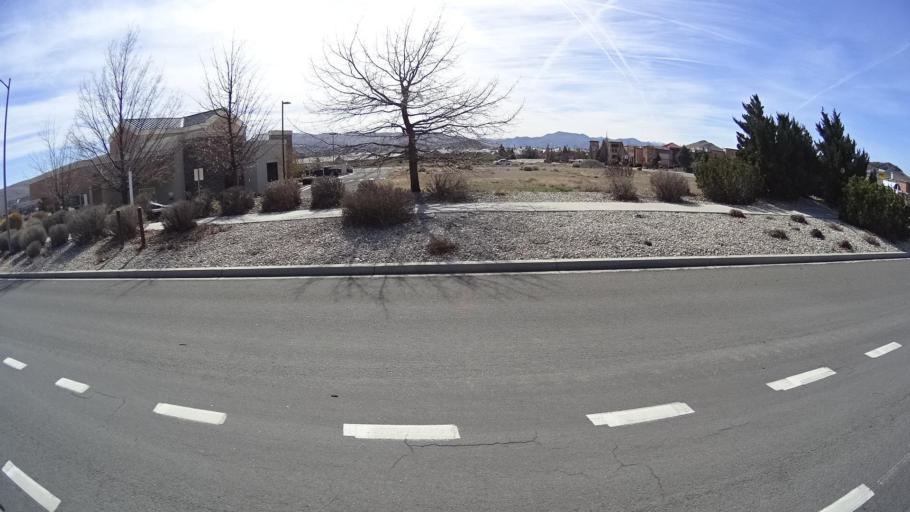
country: US
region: Nevada
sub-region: Washoe County
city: Sun Valley
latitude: 39.5848
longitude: -119.7386
